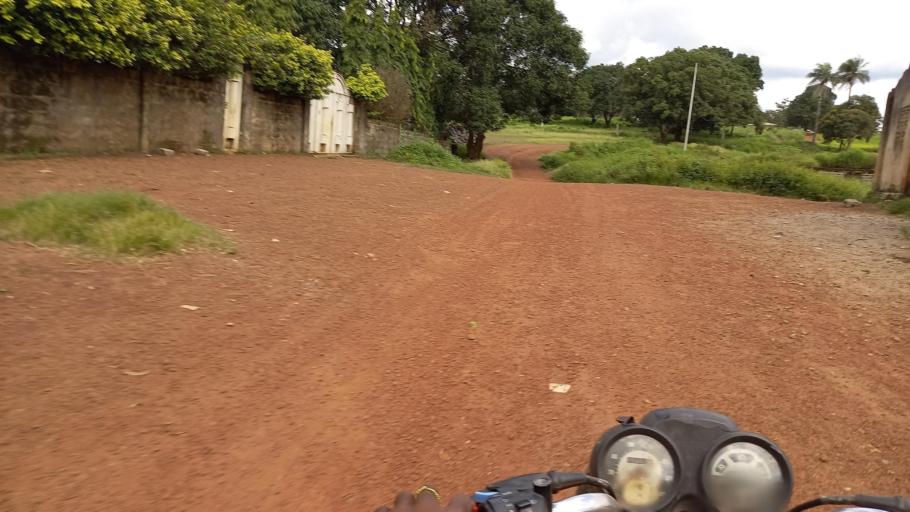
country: SL
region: Northern Province
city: Kamakwie
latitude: 9.5039
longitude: -12.2396
